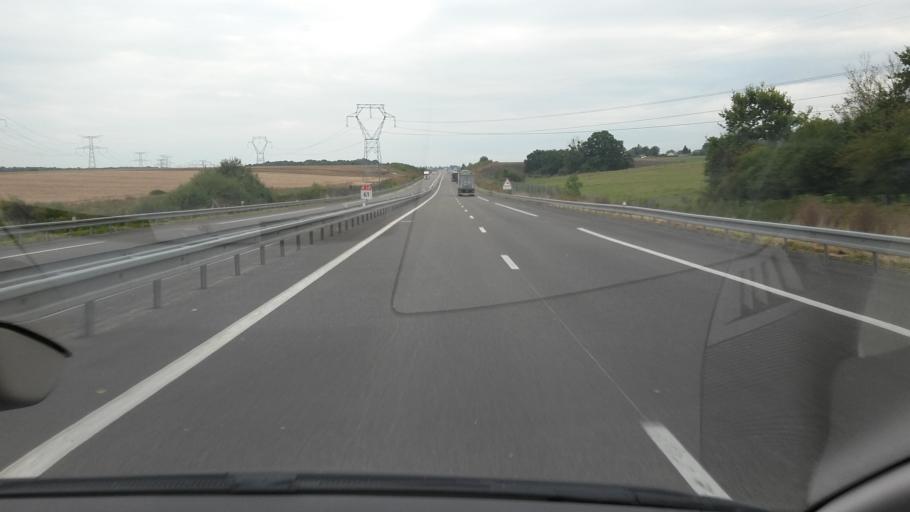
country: FR
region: Champagne-Ardenne
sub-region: Departement des Ardennes
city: Rethel
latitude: 49.5682
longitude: 4.4720
